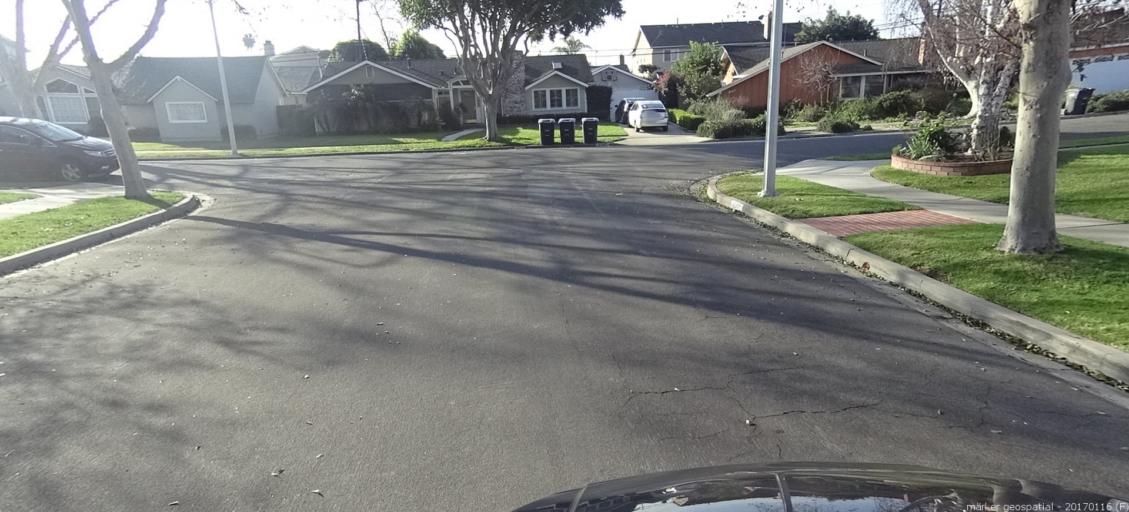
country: US
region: California
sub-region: Orange County
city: Rossmoor
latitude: 33.7856
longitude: -118.0791
